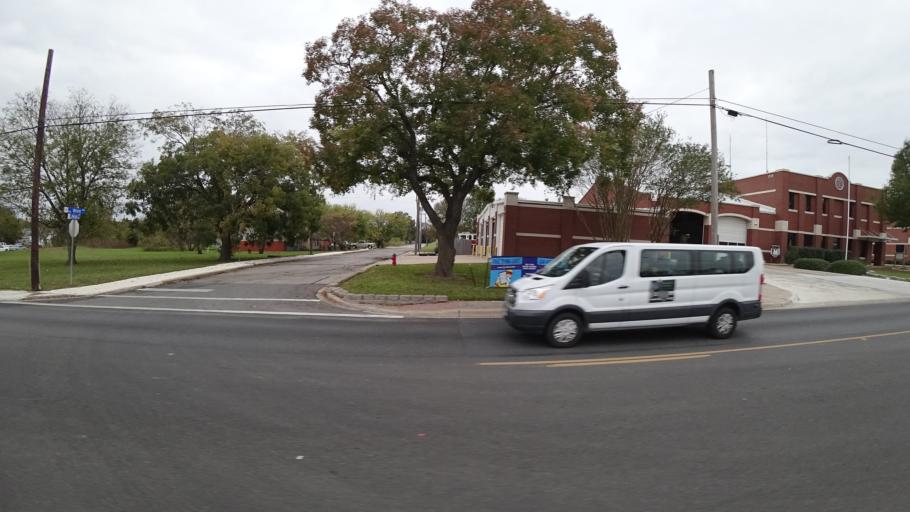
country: US
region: Texas
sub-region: Travis County
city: Pflugerville
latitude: 30.4390
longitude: -97.6190
